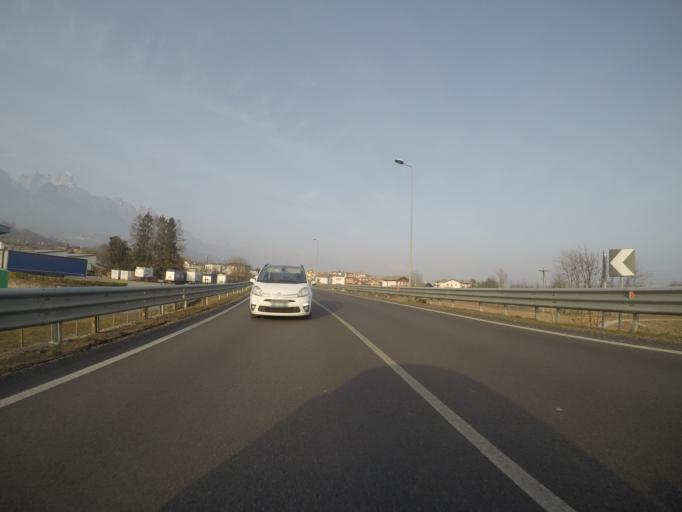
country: IT
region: Veneto
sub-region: Provincia di Belluno
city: Santa Giustina
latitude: 46.0779
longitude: 12.0324
